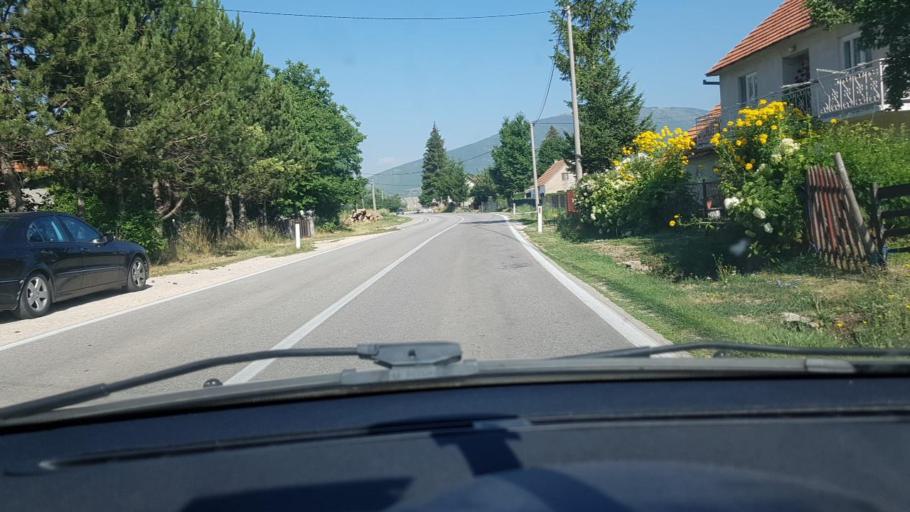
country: BA
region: Federation of Bosnia and Herzegovina
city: Zabrisce
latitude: 43.8541
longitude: 16.9455
